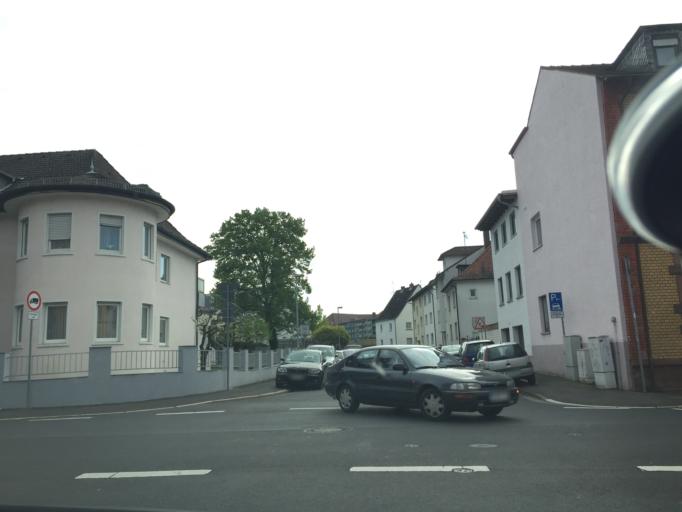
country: DE
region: Bavaria
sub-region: Regierungsbezirk Unterfranken
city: Aschaffenburg
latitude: 49.9821
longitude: 9.1351
